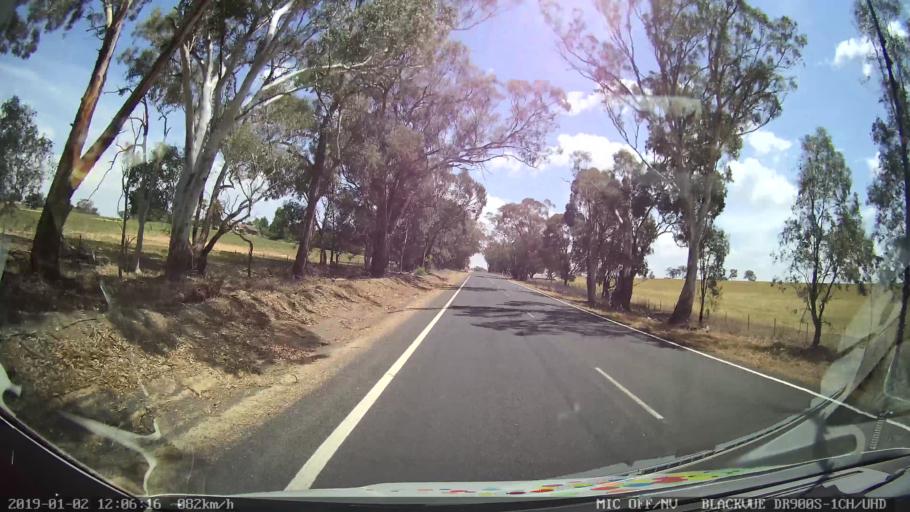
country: AU
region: New South Wales
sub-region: Young
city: Young
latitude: -34.5049
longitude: 148.2959
